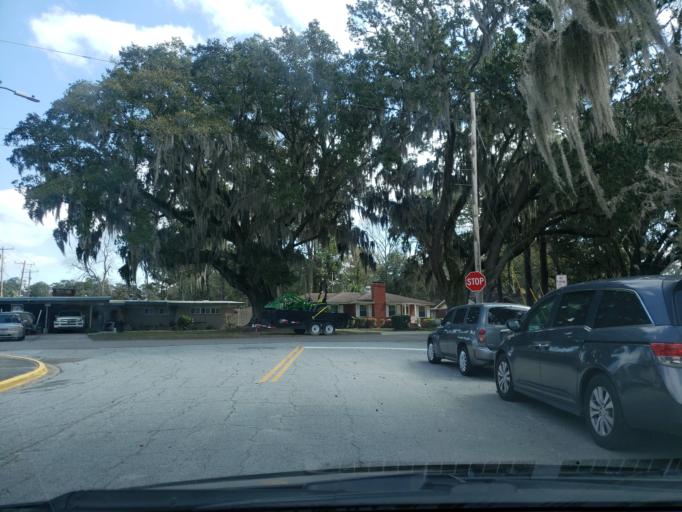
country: US
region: Georgia
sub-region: Chatham County
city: Thunderbolt
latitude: 32.0257
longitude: -81.1076
